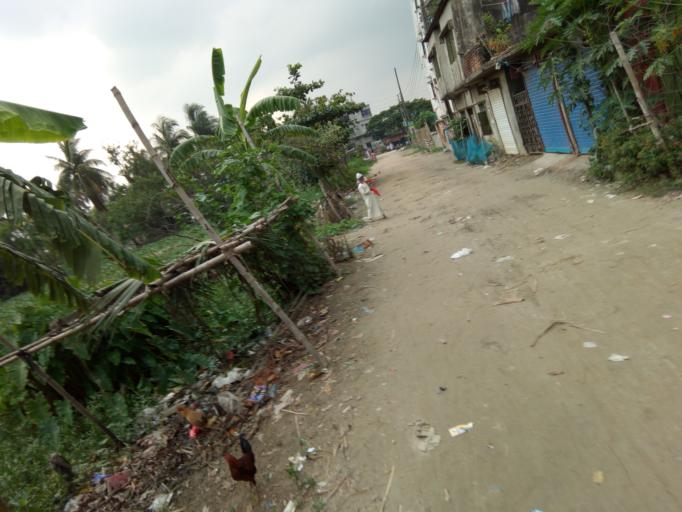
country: BD
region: Dhaka
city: Paltan
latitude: 23.7064
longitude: 90.4861
